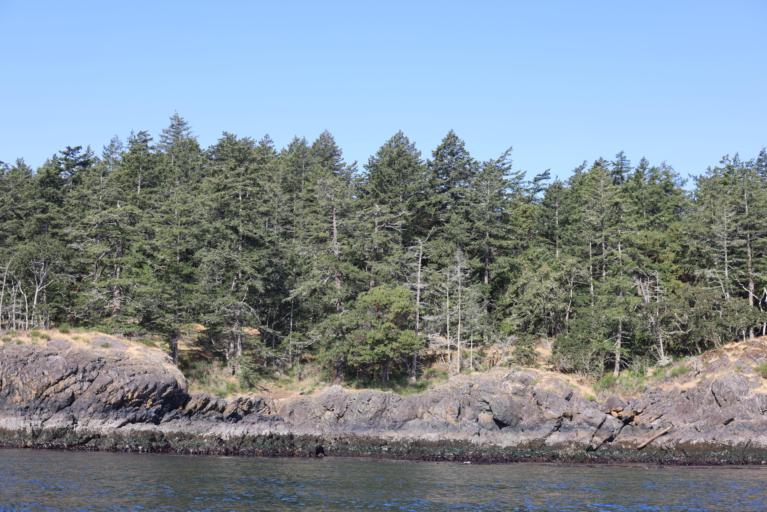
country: CA
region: British Columbia
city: Metchosin
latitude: 48.3464
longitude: -123.5387
